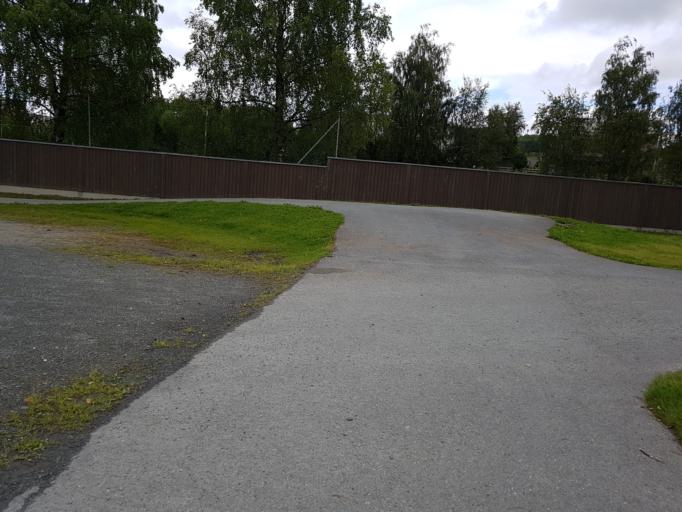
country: NO
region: Sor-Trondelag
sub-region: Trondheim
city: Trondheim
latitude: 63.3900
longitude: 10.4275
